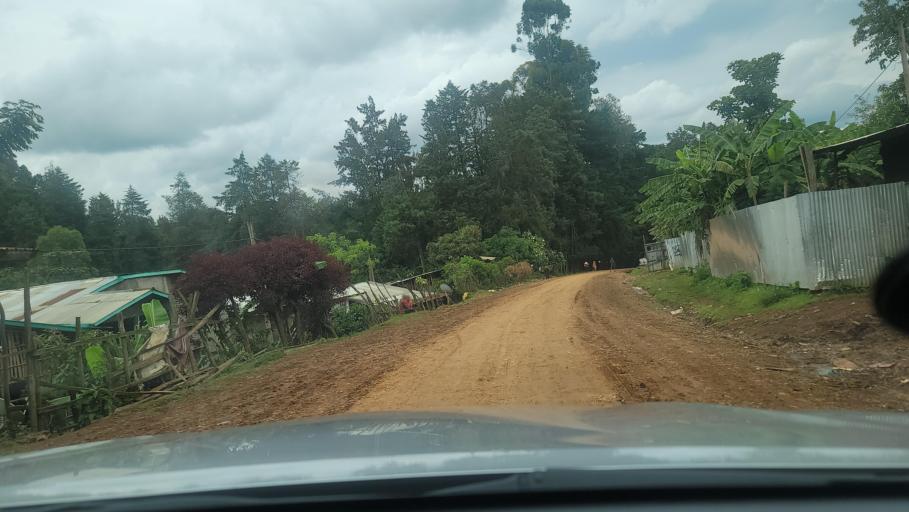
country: ET
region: Oromiya
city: Agaro
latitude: 7.7882
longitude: 36.4225
